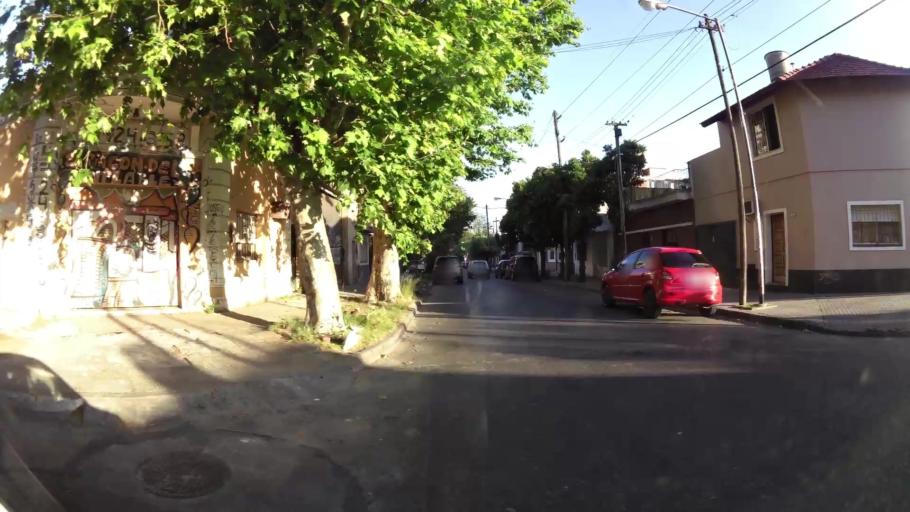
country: AR
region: Buenos Aires
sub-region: Partido de General San Martin
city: General San Martin
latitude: -34.5689
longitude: -58.5456
